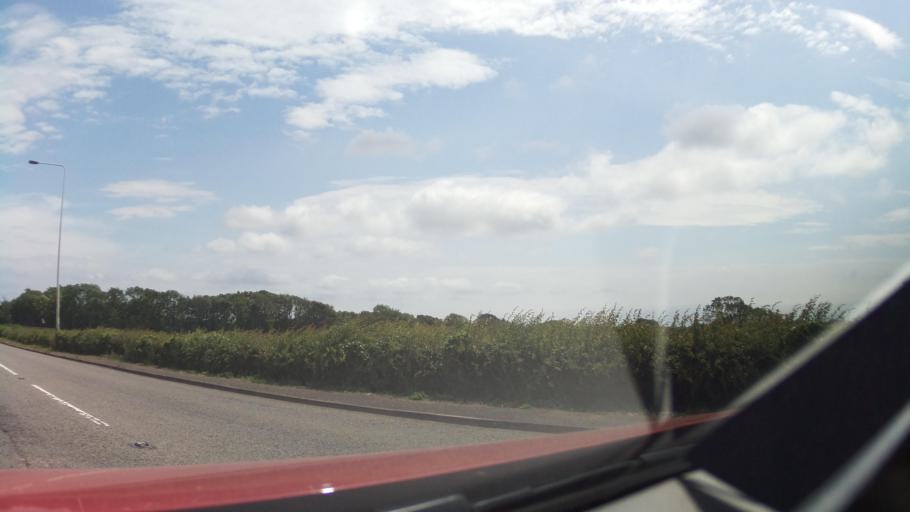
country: GB
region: Wales
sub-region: Vale of Glamorgan
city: Llangan
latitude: 51.4765
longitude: -3.5112
